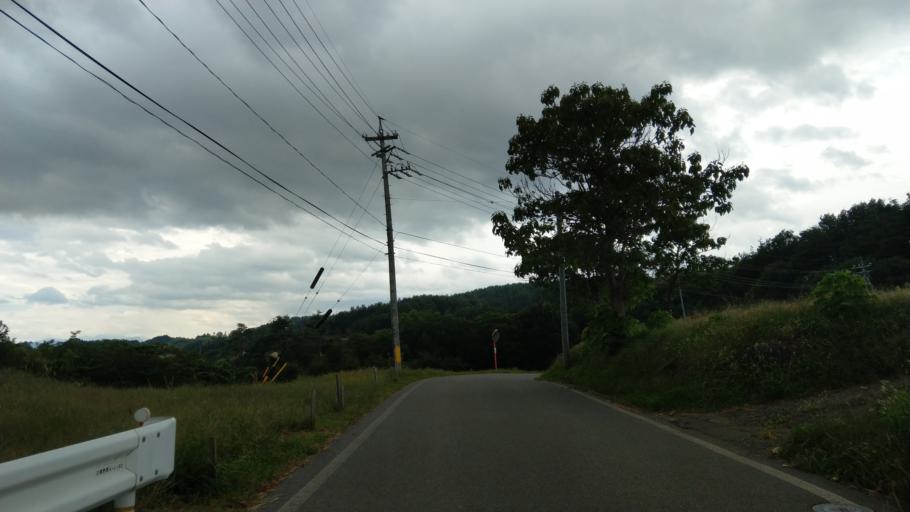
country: JP
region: Nagano
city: Komoro
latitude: 36.3121
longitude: 138.3932
